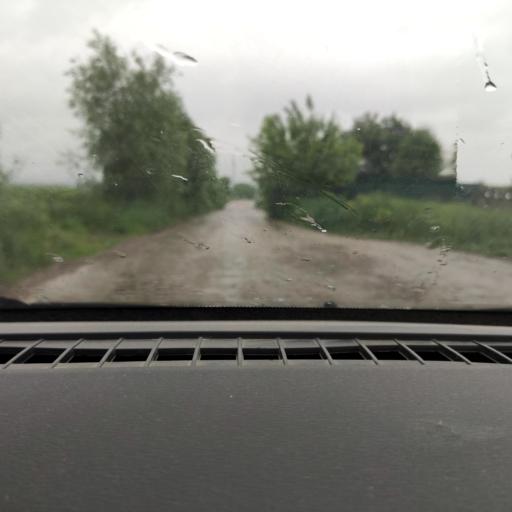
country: RU
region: Perm
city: Perm
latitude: 58.0344
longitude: 56.3604
